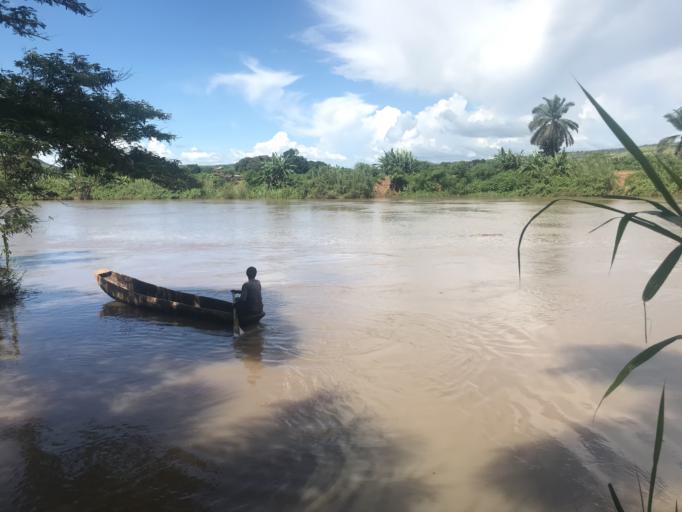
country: TZ
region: Kigoma
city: Kigoma
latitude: -5.2050
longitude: 29.8591
